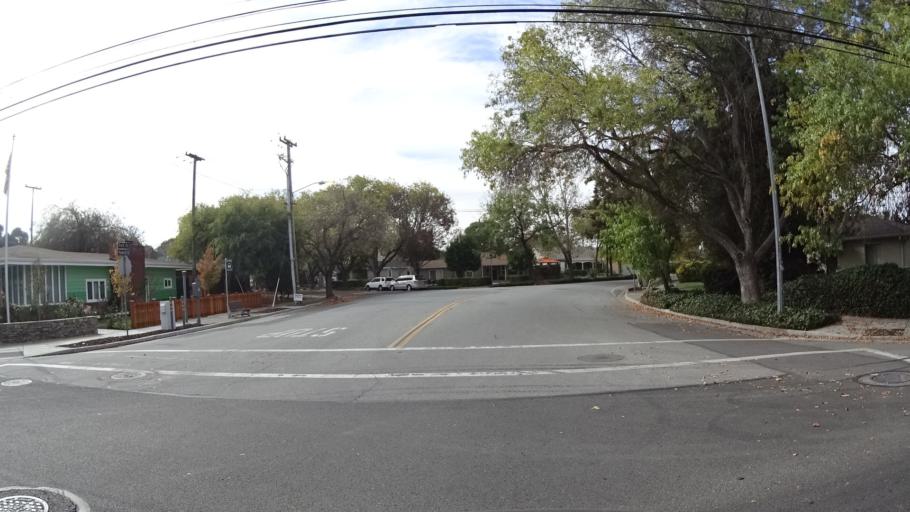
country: US
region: California
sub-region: Santa Clara County
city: Burbank
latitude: 37.3400
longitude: -121.9312
